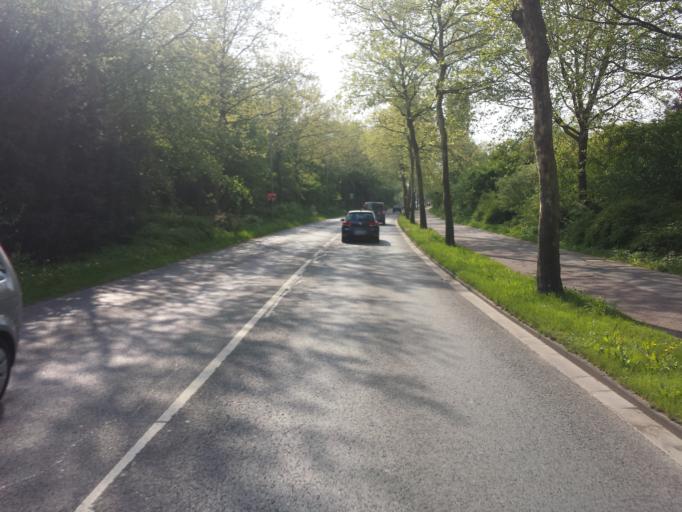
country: DE
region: North Rhine-Westphalia
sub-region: Regierungsbezirk Detmold
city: Guetersloh
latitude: 51.8840
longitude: 8.3810
